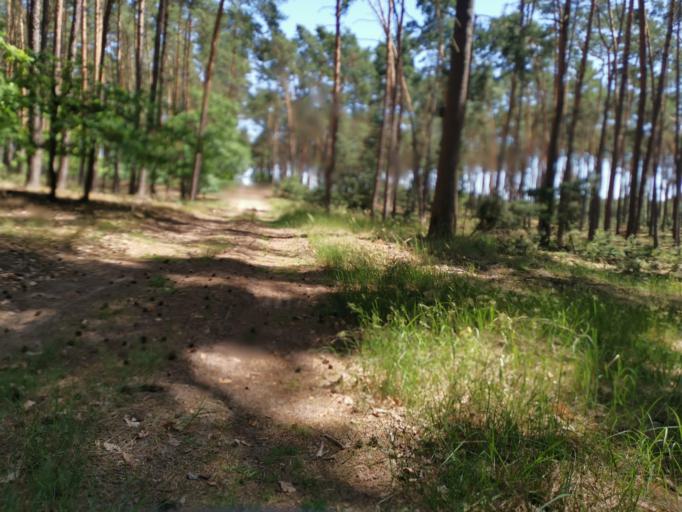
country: CZ
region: South Moravian
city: Bzenec
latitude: 48.9422
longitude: 17.2466
